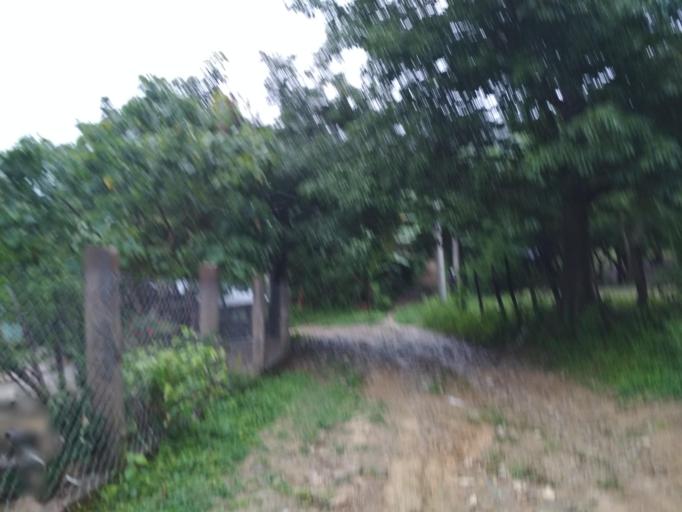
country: MX
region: Veracruz
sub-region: Chalma
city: San Pedro Coyutla
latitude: 21.1860
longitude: -98.4330
